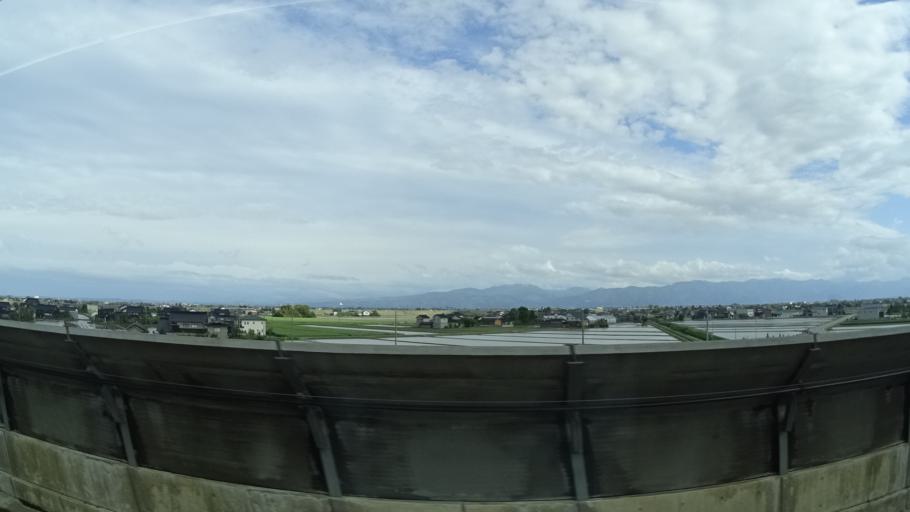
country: JP
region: Toyama
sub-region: Oyabe Shi
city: Oyabe
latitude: 36.6778
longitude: 136.9049
